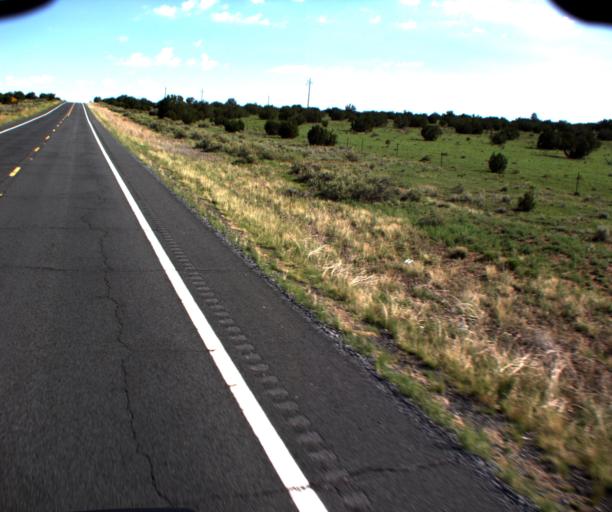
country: US
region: Arizona
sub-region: Coconino County
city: Williams
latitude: 35.4966
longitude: -112.1741
